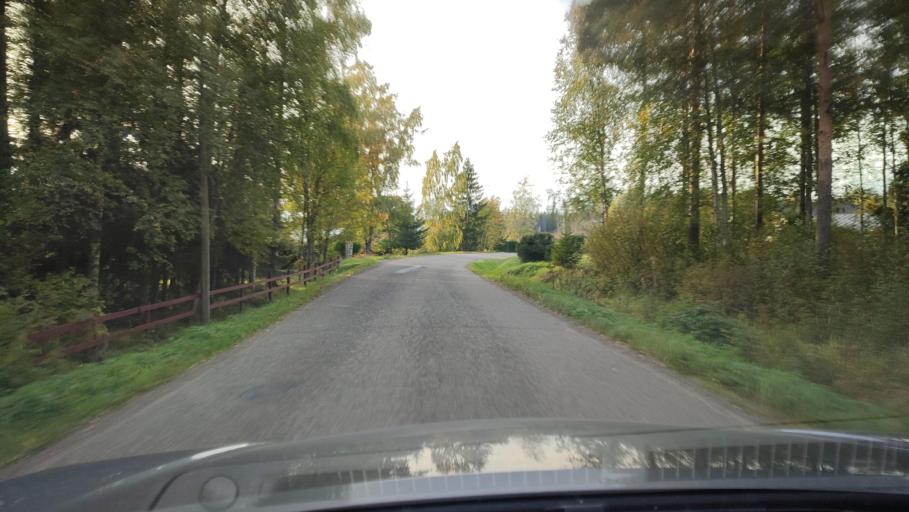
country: FI
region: Southern Ostrobothnia
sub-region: Suupohja
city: Karijoki
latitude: 62.1283
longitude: 21.5827
